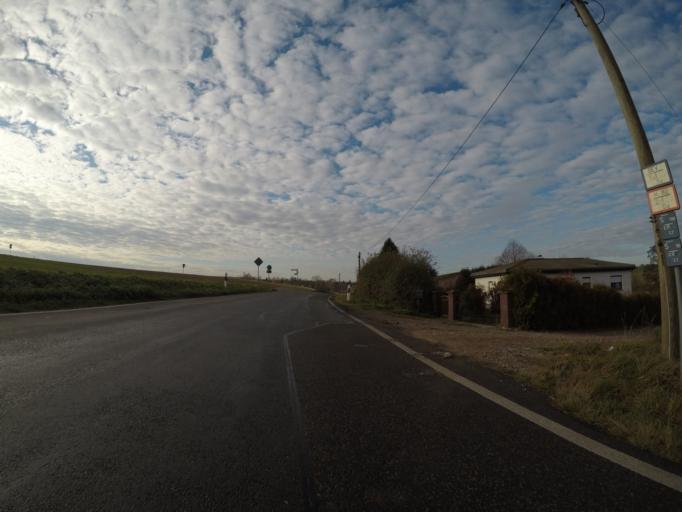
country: DE
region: Thuringia
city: Ponitz
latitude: 50.8559
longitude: 12.4087
